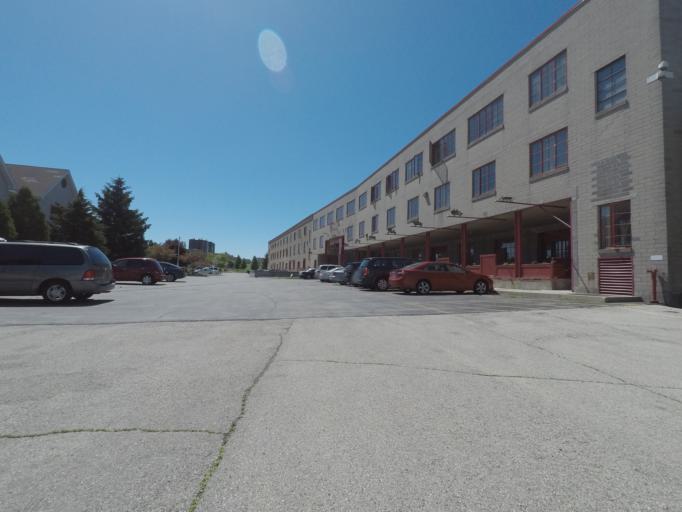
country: US
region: Wisconsin
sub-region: Sheboygan County
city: Sheboygan
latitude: 43.7539
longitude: -87.7193
